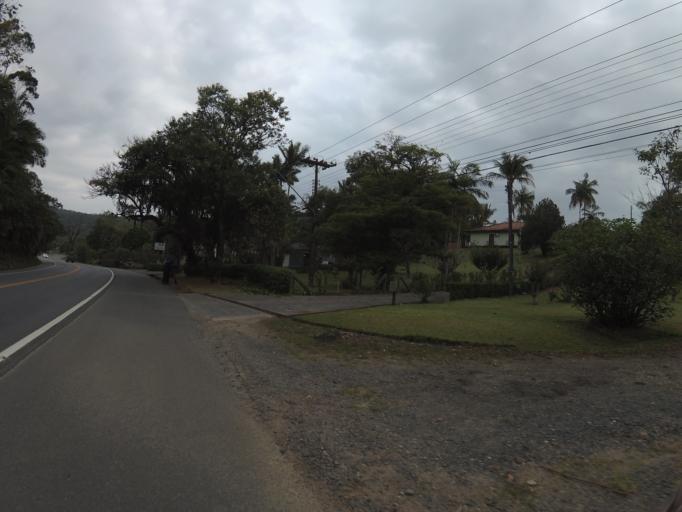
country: BR
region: Santa Catarina
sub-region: Indaial
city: Indaial
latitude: -26.8650
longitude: -49.1506
